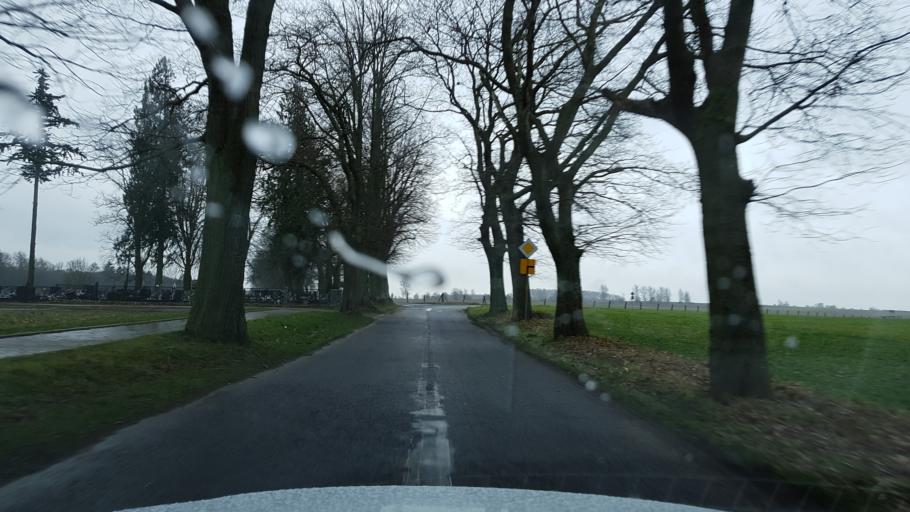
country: PL
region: West Pomeranian Voivodeship
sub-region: Powiat lobeski
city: Dobra
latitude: 53.5963
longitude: 15.3835
